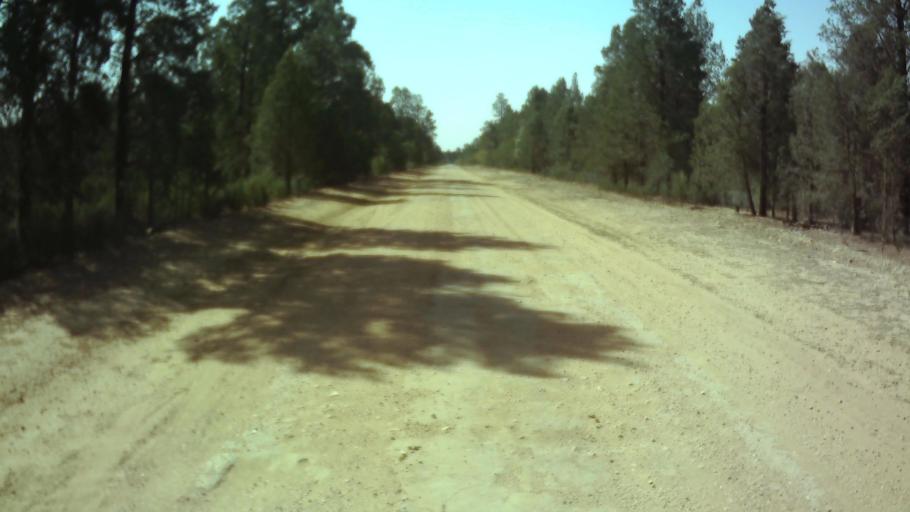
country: AU
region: New South Wales
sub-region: Weddin
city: Grenfell
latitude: -33.9160
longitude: 147.9220
